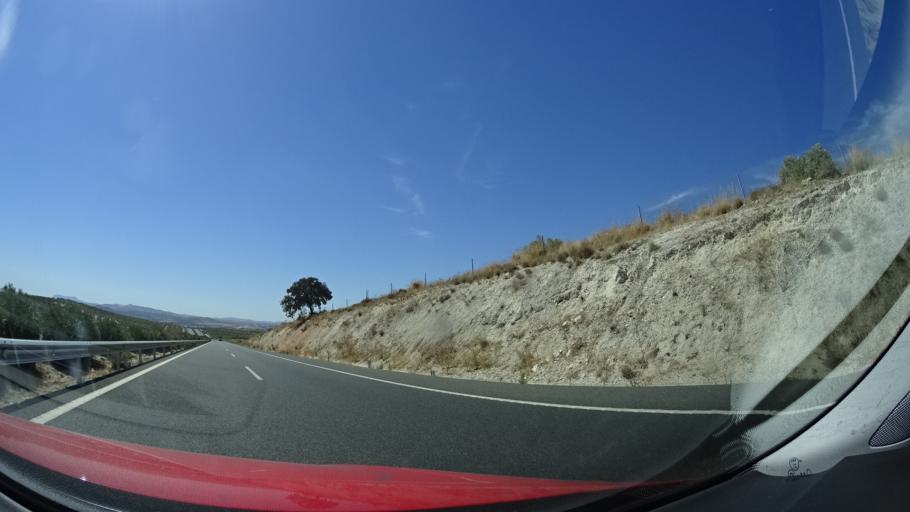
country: ES
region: Andalusia
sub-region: Provincia de Sevilla
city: Gilena
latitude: 37.2744
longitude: -4.9429
